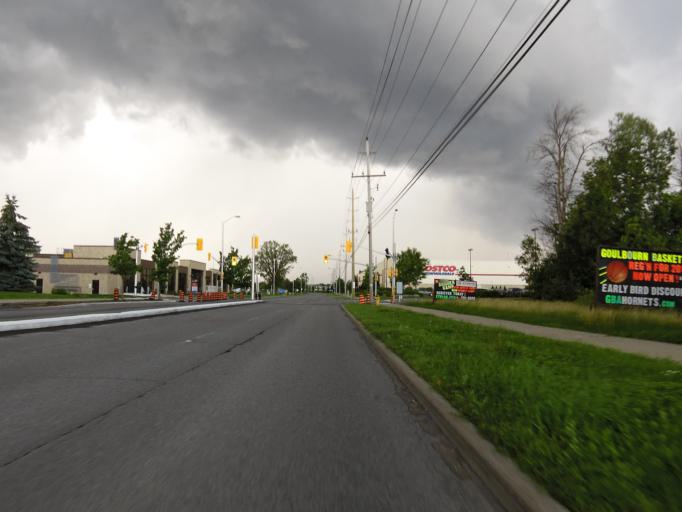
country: CA
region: Ontario
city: Bells Corners
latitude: 45.3009
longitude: -75.9120
